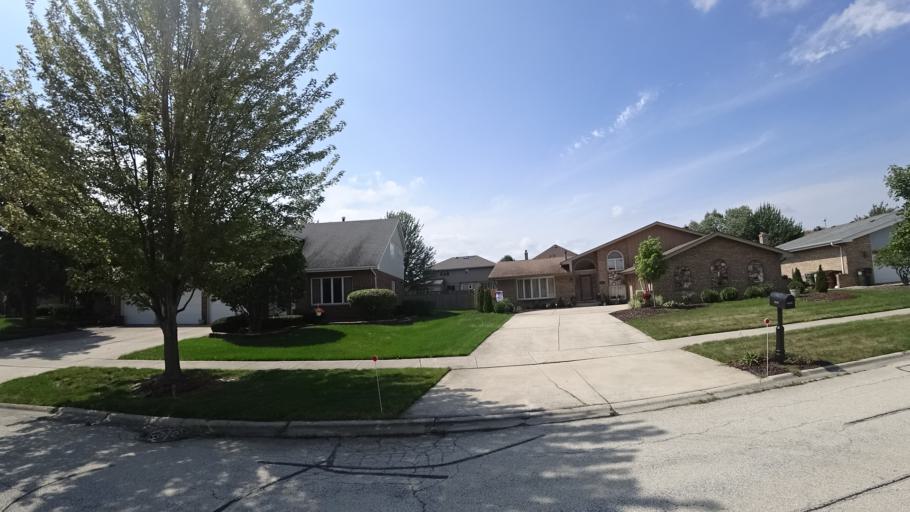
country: US
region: Illinois
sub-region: Cook County
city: Orland Hills
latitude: 41.5671
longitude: -87.8203
